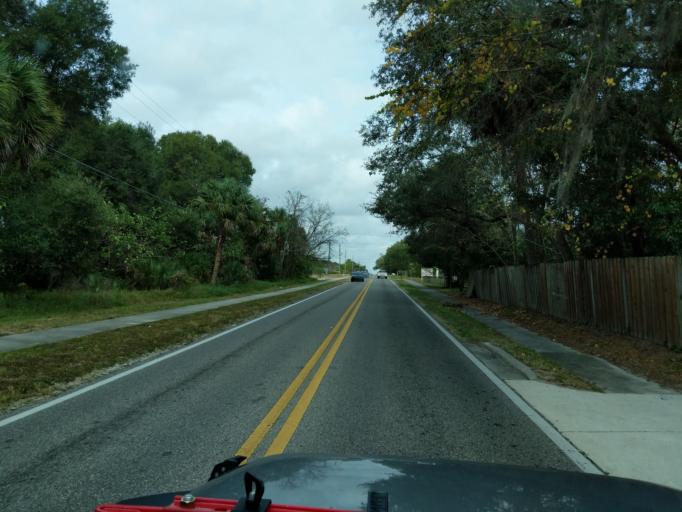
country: US
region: Florida
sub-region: Orange County
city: Paradise Heights
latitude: 28.6263
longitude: -81.5434
